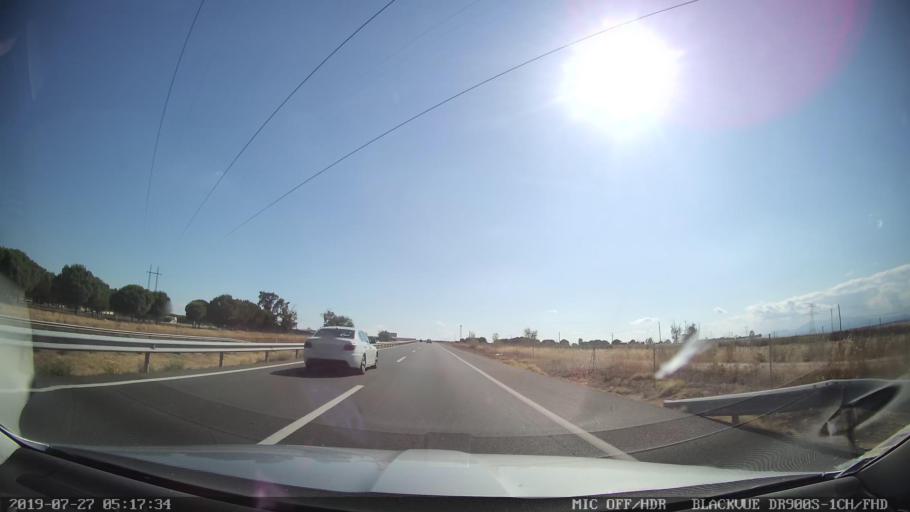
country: ES
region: Castille-La Mancha
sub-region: Province of Toledo
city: Maqueda
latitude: 40.0474
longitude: -4.3943
